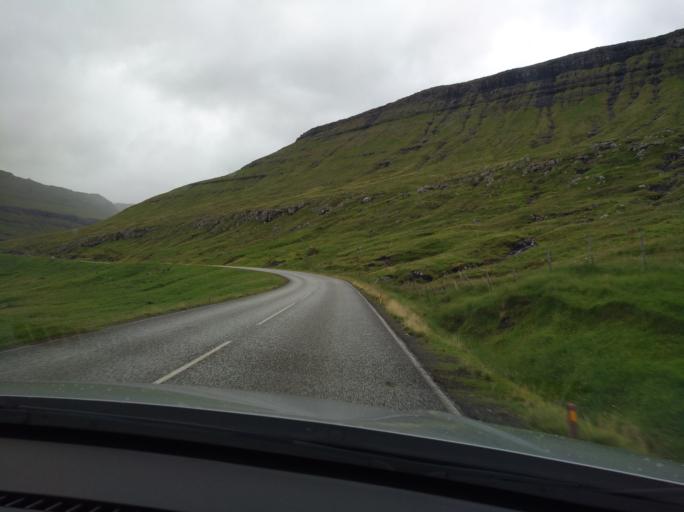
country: FO
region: Eysturoy
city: Fuglafjordur
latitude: 62.2155
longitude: -6.8635
